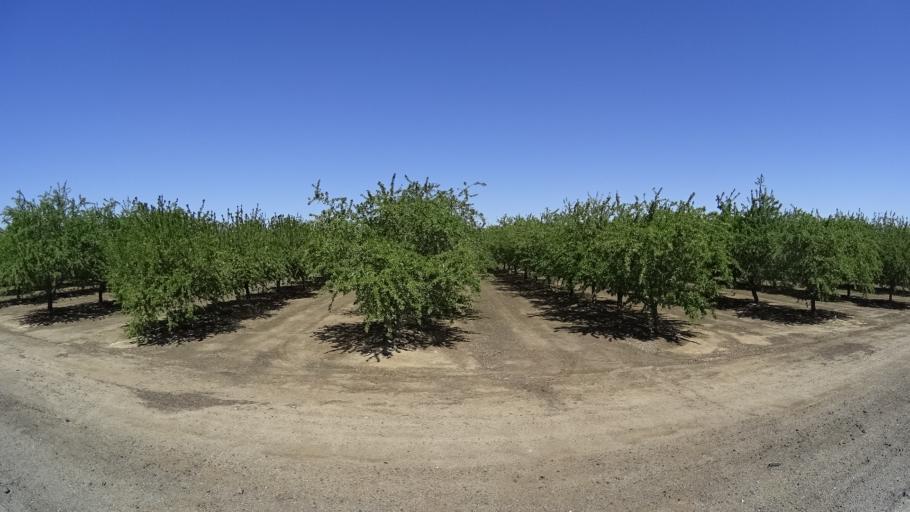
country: US
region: California
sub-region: Fresno County
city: West Park
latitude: 36.7063
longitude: -119.9109
